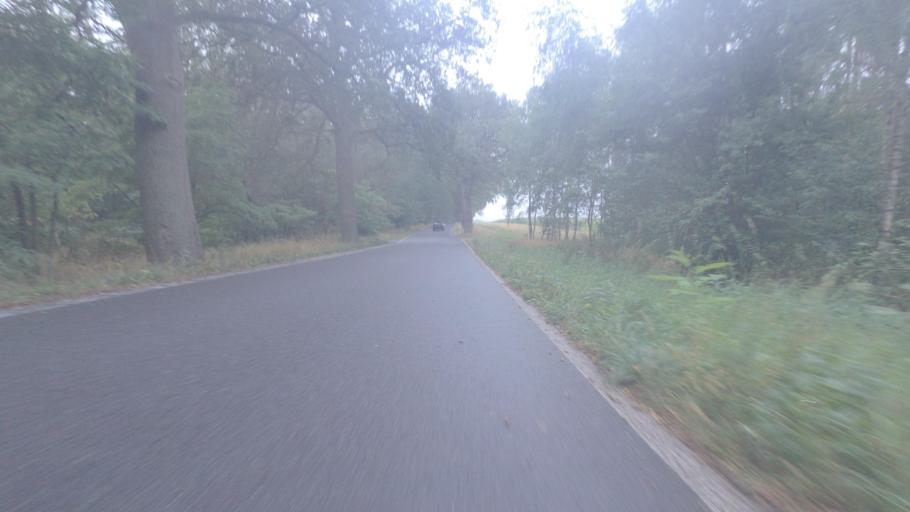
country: DE
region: Brandenburg
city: Heiligengrabe
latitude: 53.1548
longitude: 12.3446
